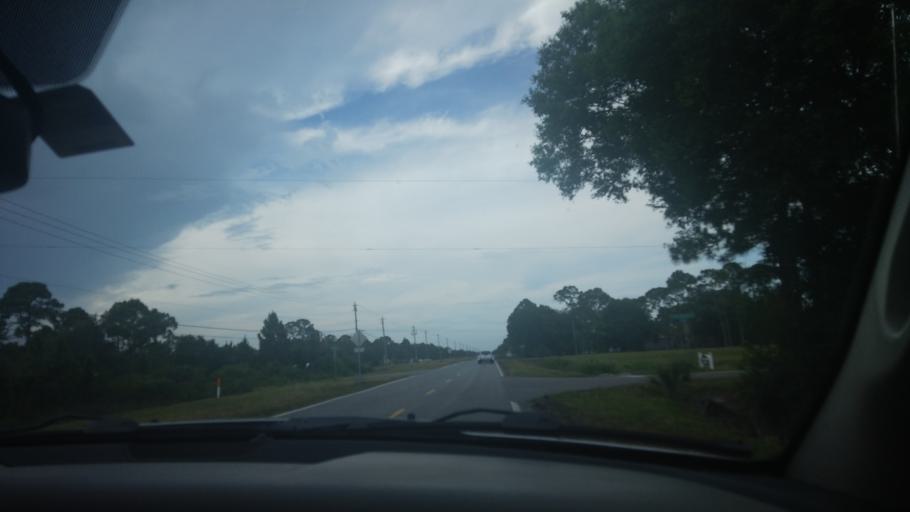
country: US
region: Florida
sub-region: Brevard County
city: Grant-Valkaria
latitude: 27.9161
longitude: -80.6230
